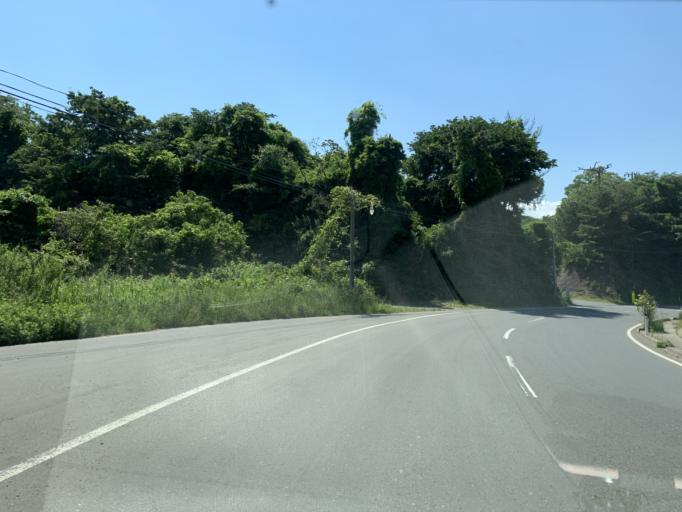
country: JP
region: Miyagi
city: Matsushima
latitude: 38.3358
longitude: 141.1509
